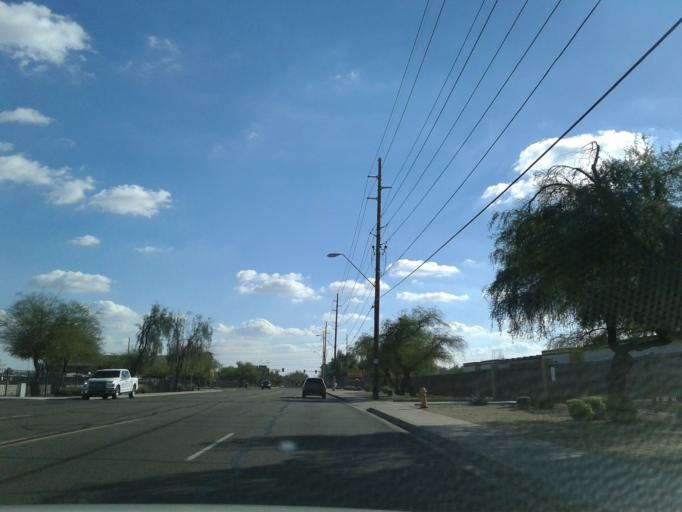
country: US
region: Arizona
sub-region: Maricopa County
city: Peoria
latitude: 33.6788
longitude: -112.1174
